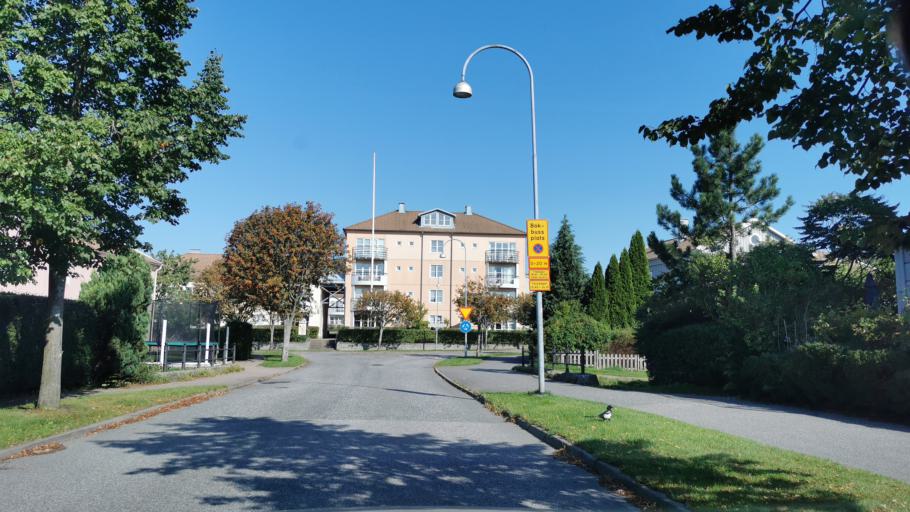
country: SE
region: Vaestra Goetaland
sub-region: Molndal
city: Moelndal
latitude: 57.6545
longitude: 11.9625
